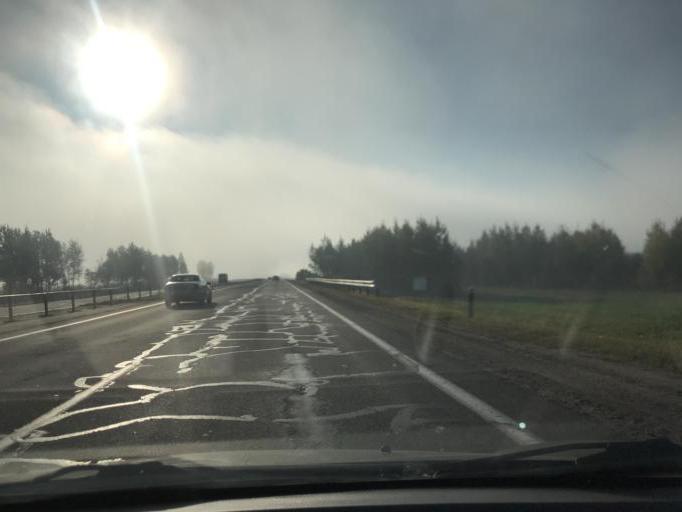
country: BY
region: Minsk
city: Luhavaya Slabada
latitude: 53.7316
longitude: 27.8516
